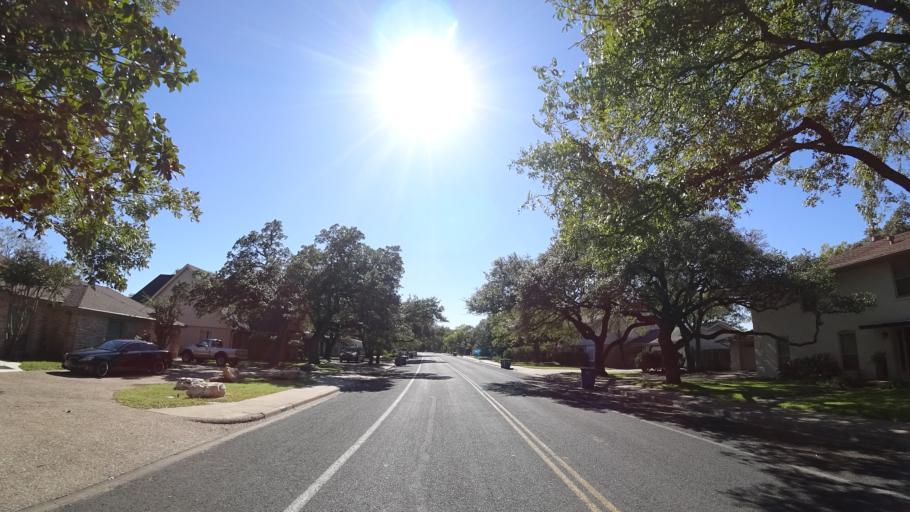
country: US
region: Texas
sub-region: Travis County
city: West Lake Hills
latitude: 30.3542
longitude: -97.7703
